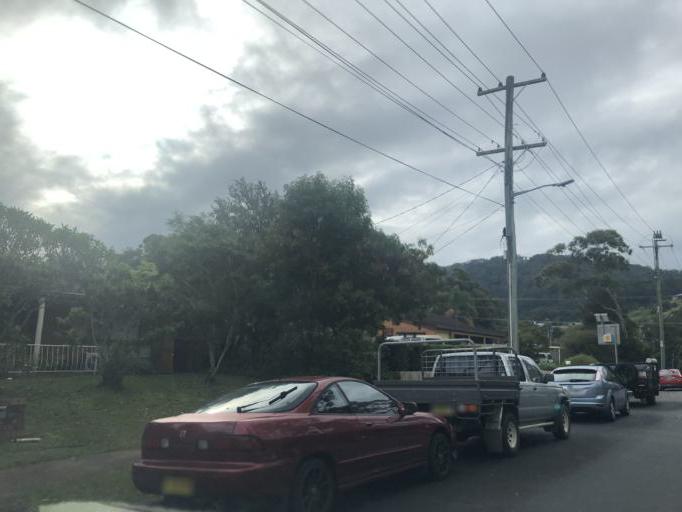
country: AU
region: New South Wales
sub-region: Coffs Harbour
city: Coffs Harbour
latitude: -30.2823
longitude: 153.1118
